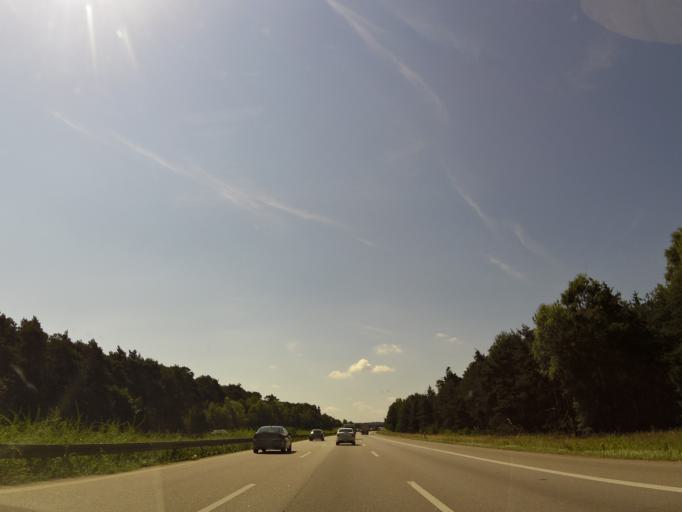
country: DE
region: Bavaria
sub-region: Upper Bavaria
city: Reichertshofen
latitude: 48.6652
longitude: 11.5101
